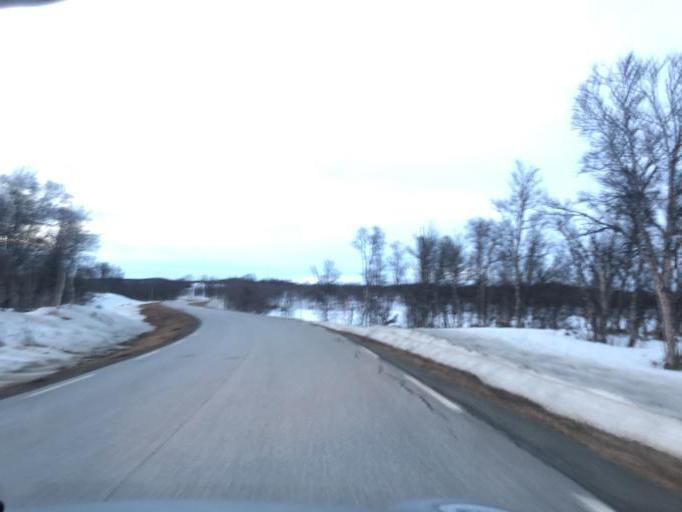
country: NO
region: Sor-Trondelag
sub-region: Tydal
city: Aas
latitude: 62.7225
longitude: 11.8266
